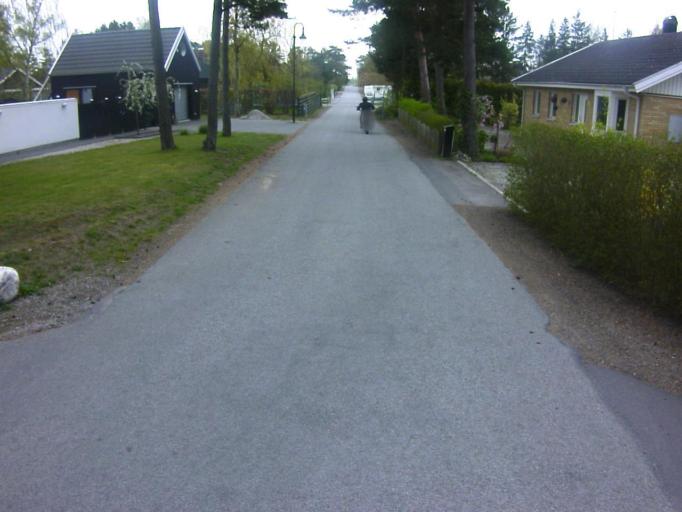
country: SE
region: Skane
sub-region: Kavlinge Kommun
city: Loddekopinge
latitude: 55.7532
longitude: 12.9929
